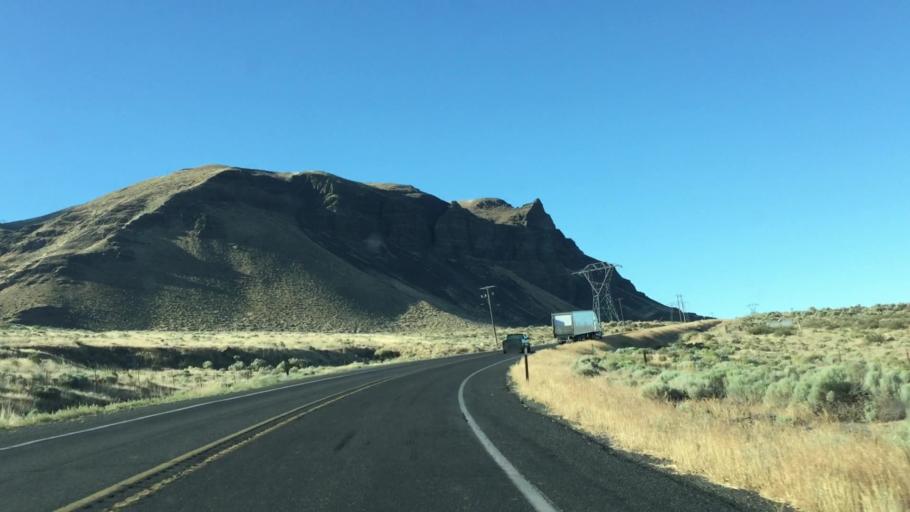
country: US
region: Washington
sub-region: Grant County
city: Mattawa
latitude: 46.8141
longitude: -119.9196
